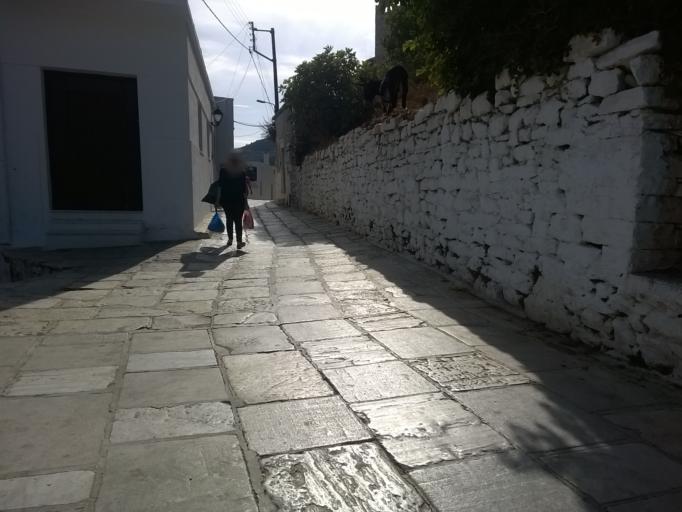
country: GR
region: South Aegean
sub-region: Nomos Kykladon
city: Filotion
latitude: 37.0720
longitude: 25.5213
